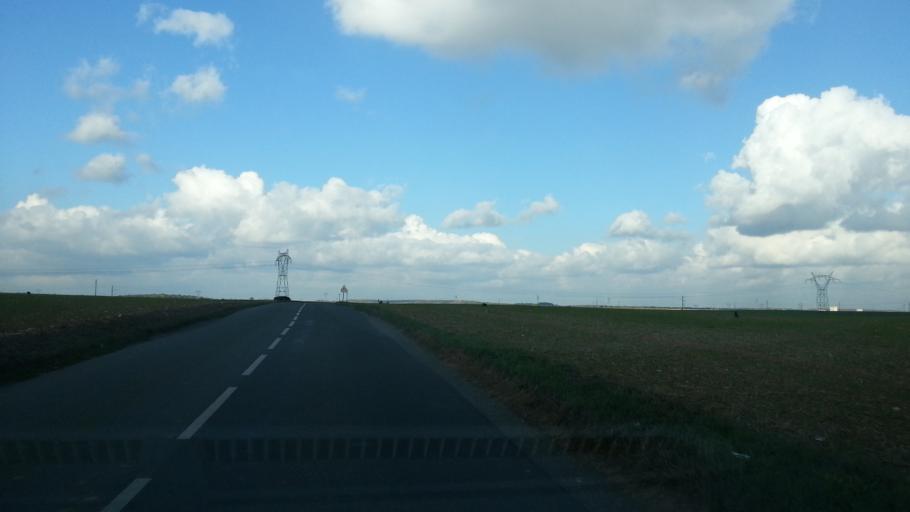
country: FR
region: Picardie
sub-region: Departement de l'Oise
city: Villers-sous-Saint-Leu
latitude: 49.2268
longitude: 2.4140
